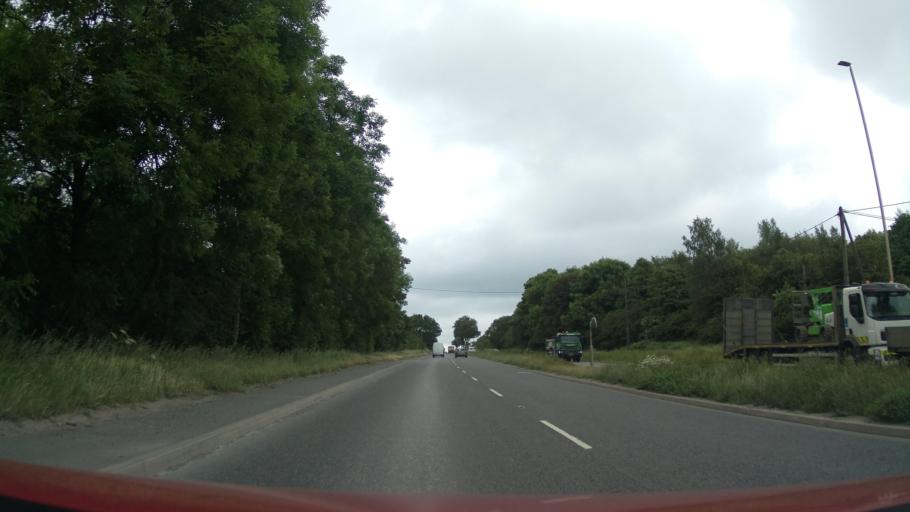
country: GB
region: England
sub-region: Leicestershire
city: Markfield
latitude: 52.7018
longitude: -1.3143
